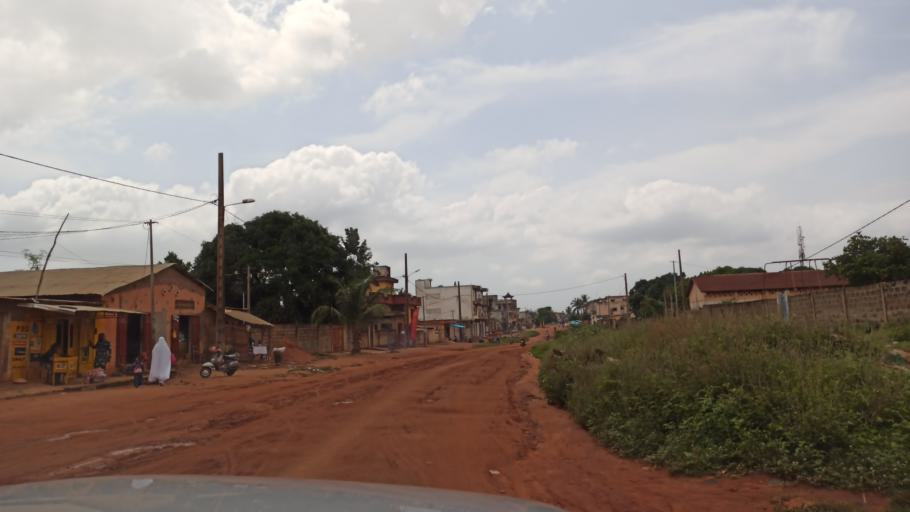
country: BJ
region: Queme
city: Porto-Novo
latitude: 6.4996
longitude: 2.6311
